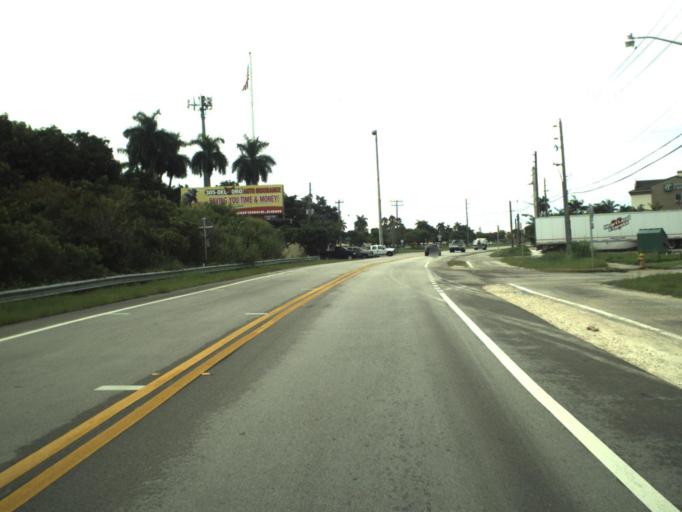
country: US
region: Florida
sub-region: Miami-Dade County
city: Florida City
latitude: 25.4378
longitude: -80.4759
